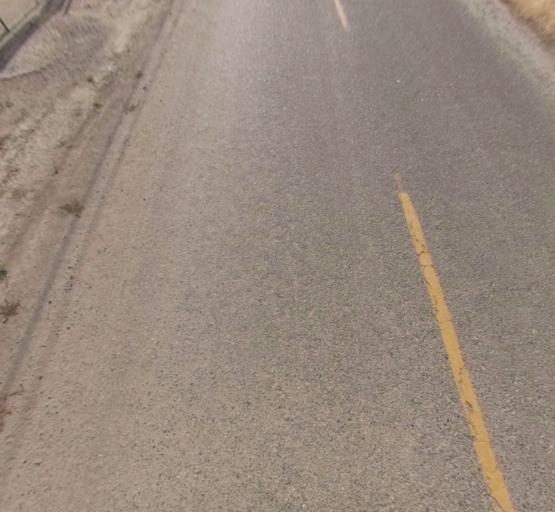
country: US
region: California
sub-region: Madera County
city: Madera
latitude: 36.9311
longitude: -120.1131
